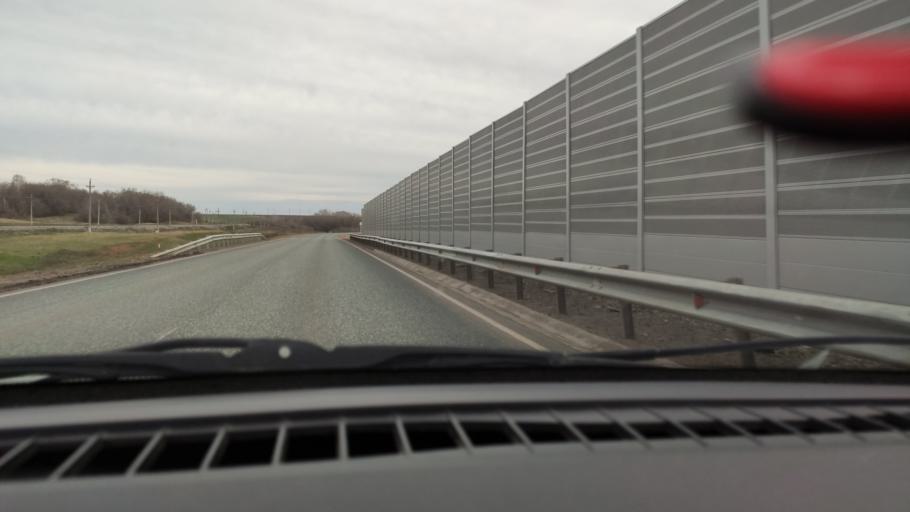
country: RU
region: Bashkortostan
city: Yermolayevo
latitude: 52.4775
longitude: 55.8306
